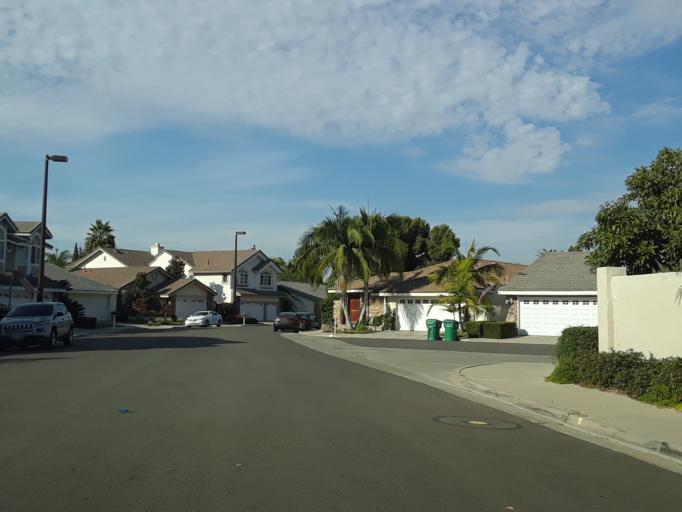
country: US
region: California
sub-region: Orange County
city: Irvine
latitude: 33.6864
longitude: -117.7961
